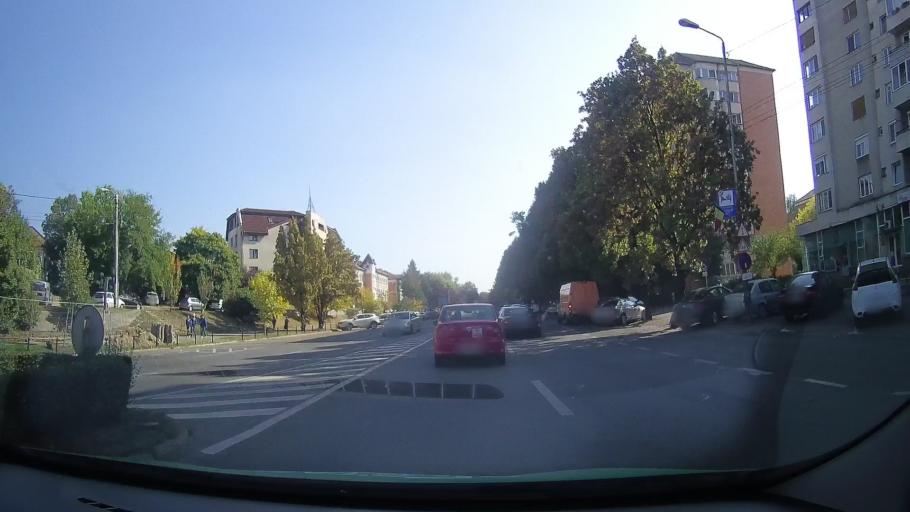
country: RO
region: Bihor
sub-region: Comuna Biharea
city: Oradea
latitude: 47.0688
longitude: 21.9258
